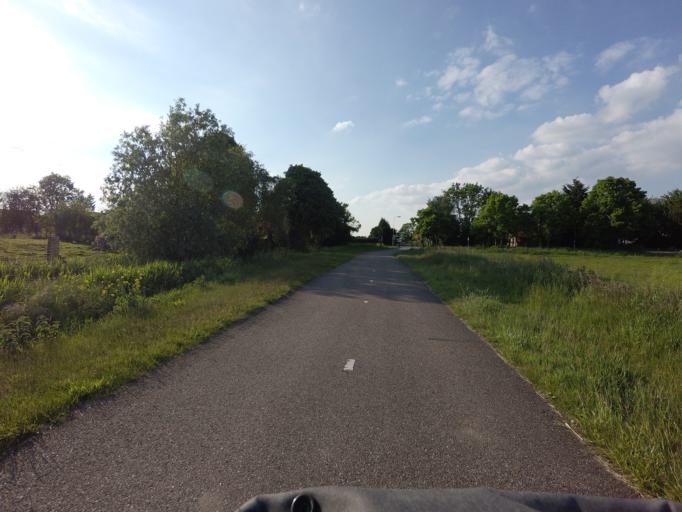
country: NL
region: South Holland
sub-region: Gemeente Rijnwoude
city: Benthuizen
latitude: 52.0412
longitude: 4.5632
